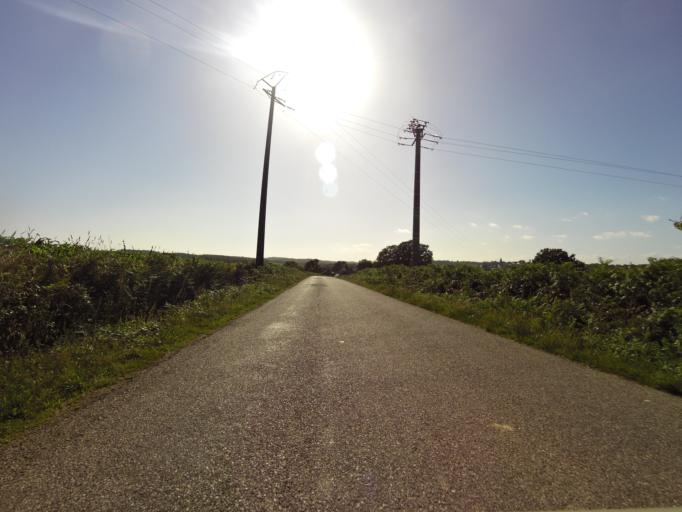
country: FR
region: Brittany
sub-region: Departement du Morbihan
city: Limerzel
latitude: 47.6287
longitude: -2.3364
